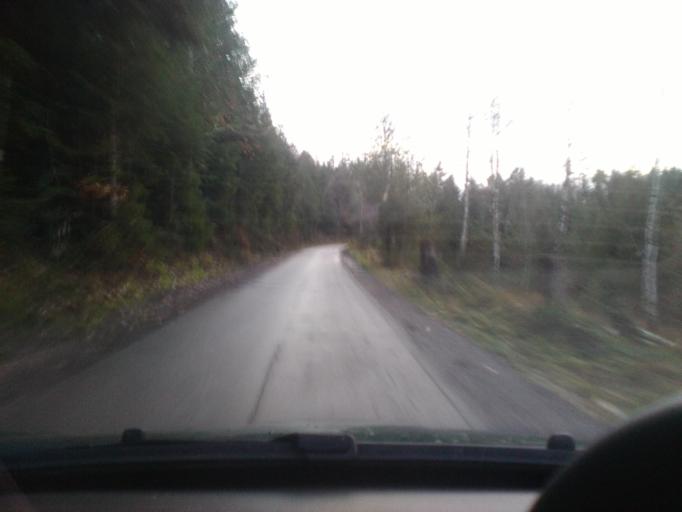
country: FR
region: Lorraine
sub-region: Departement des Vosges
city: Corcieux
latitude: 48.2075
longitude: 6.9005
